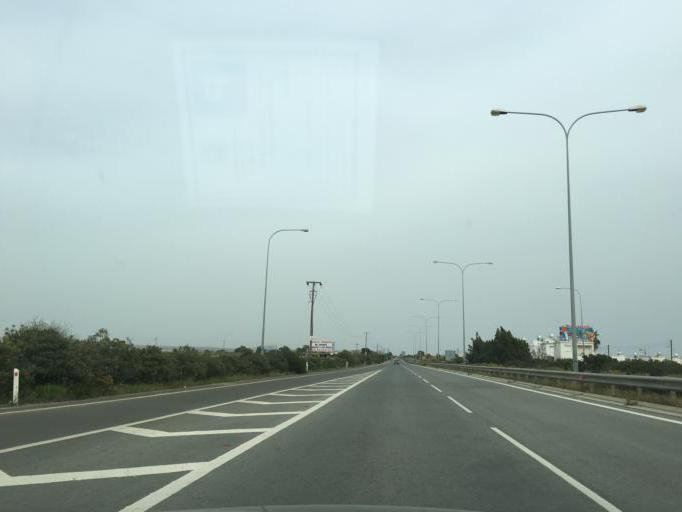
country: CY
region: Ammochostos
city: Liopetri
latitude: 34.9780
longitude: 33.8965
